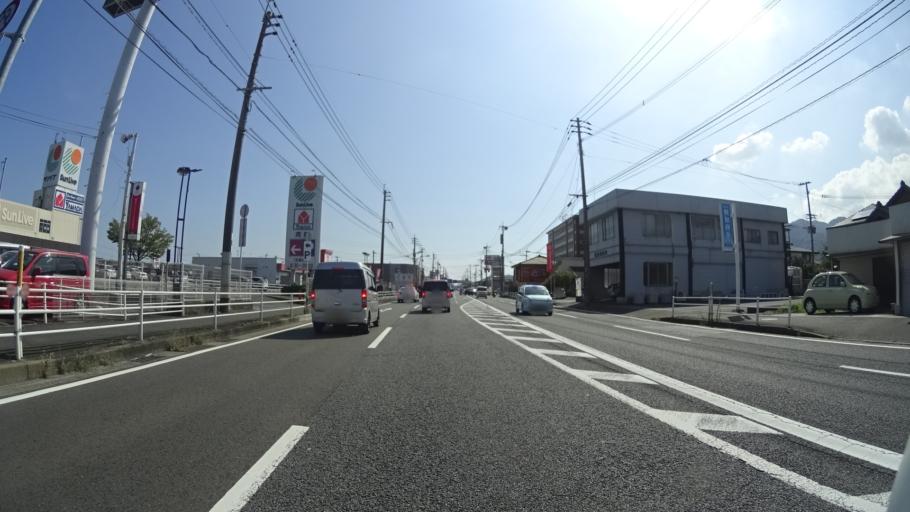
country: JP
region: Fukuoka
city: Kanda
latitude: 33.7746
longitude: 130.9824
